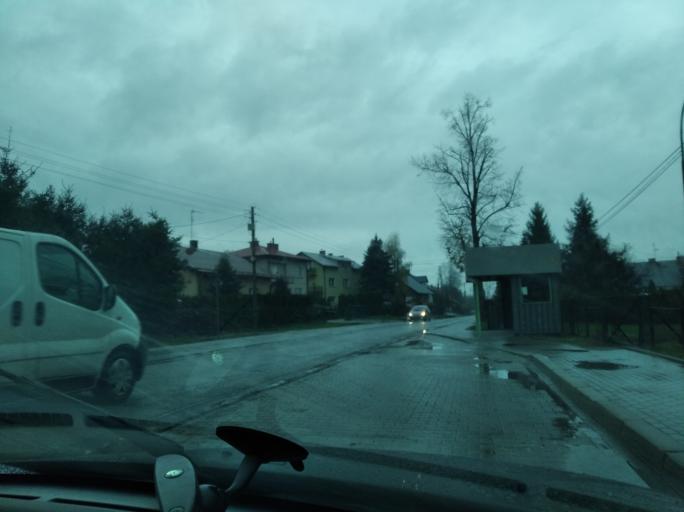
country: PL
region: Subcarpathian Voivodeship
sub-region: Powiat lancucki
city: Albigowa
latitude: 50.0175
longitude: 22.2249
